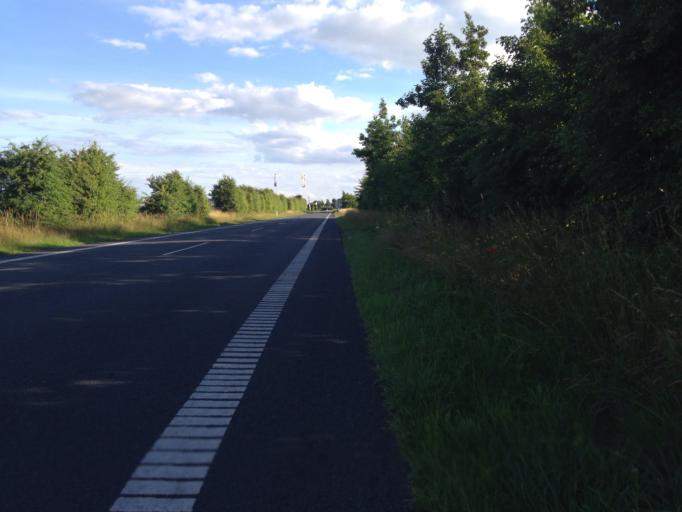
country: DK
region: South Denmark
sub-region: Middelfart Kommune
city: Norre Aby
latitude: 55.4771
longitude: 9.8997
